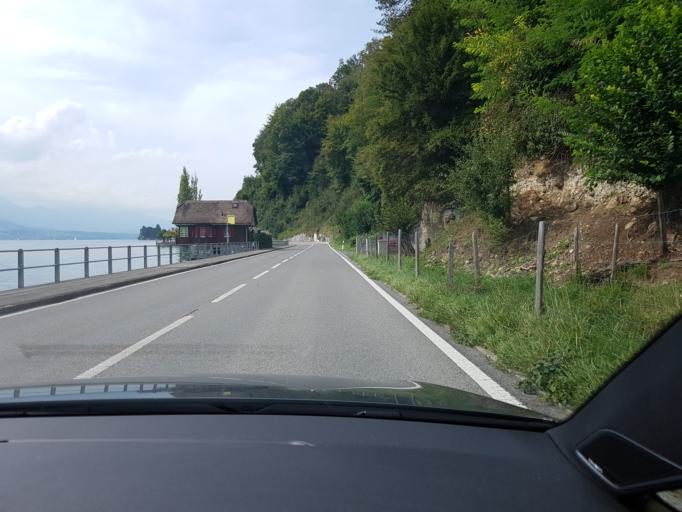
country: CH
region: Bern
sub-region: Thun District
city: Sigriswil
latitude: 46.7090
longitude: 7.7186
